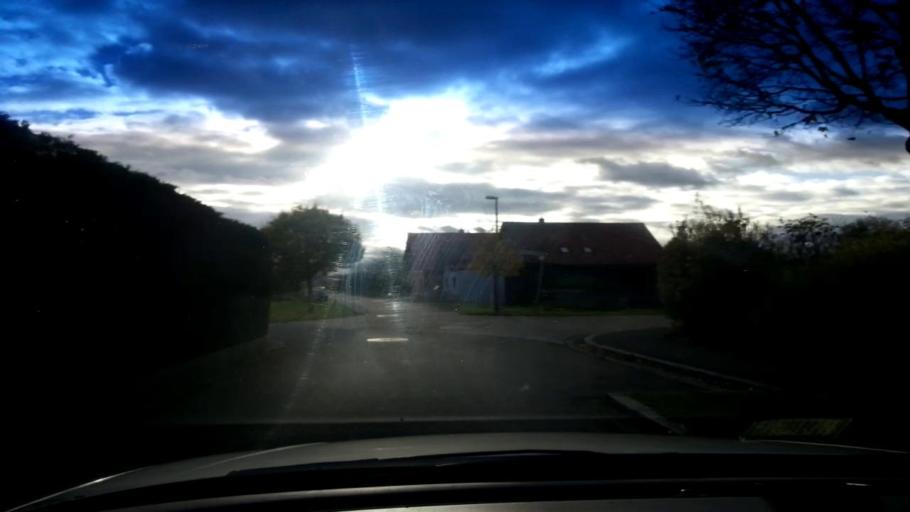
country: DE
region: Bavaria
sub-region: Upper Franconia
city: Rattelsdorf
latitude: 50.0069
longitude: 10.9005
